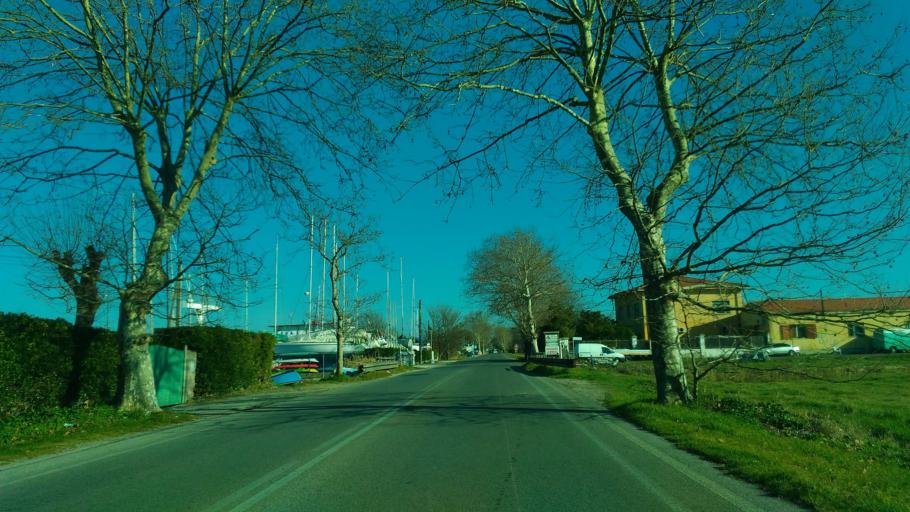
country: IT
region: Tuscany
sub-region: Province of Pisa
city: Marina di Pisa
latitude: 43.6792
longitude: 10.2826
